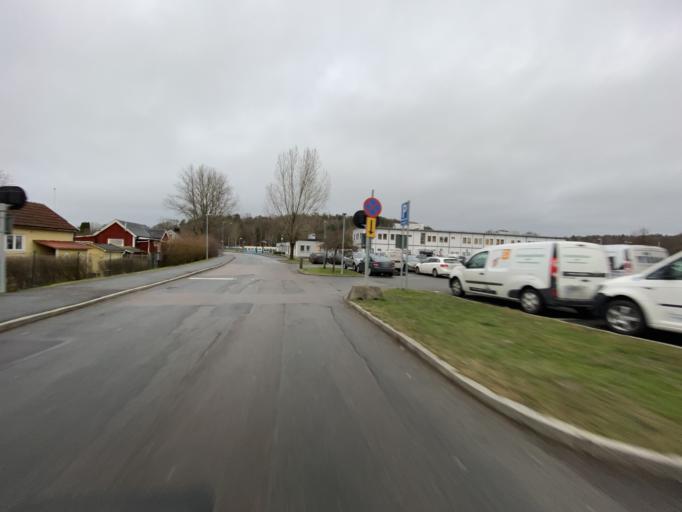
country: SE
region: Vaestra Goetaland
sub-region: Goteborg
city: Eriksbo
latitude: 57.7215
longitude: 12.0474
